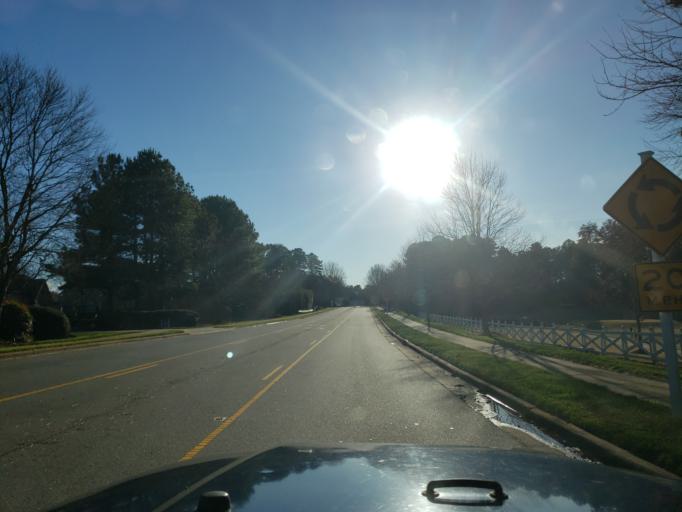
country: US
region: North Carolina
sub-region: Catawba County
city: Lake Norman of Catawba
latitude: 35.5367
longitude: -80.9186
